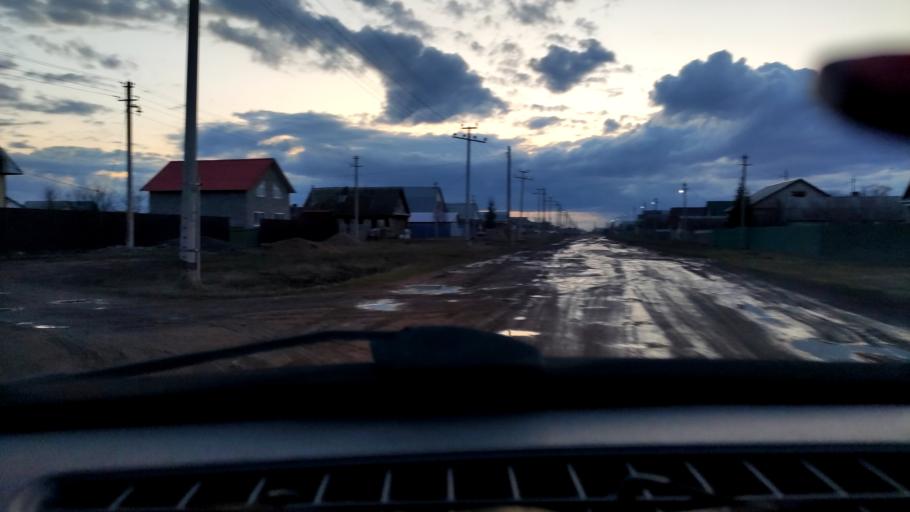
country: RU
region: Bashkortostan
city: Ulukulevo
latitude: 54.4203
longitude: 56.3393
